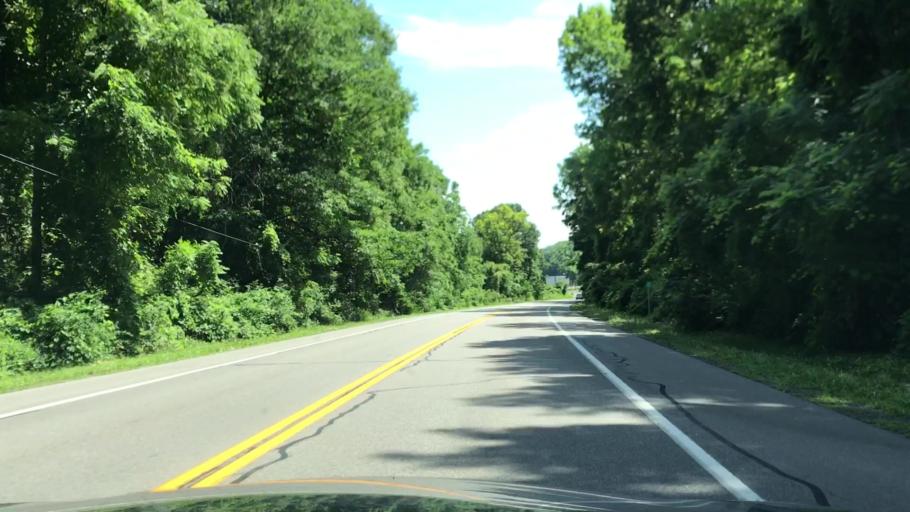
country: US
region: New York
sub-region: Livingston County
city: Mount Morris
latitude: 42.7504
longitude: -77.8832
